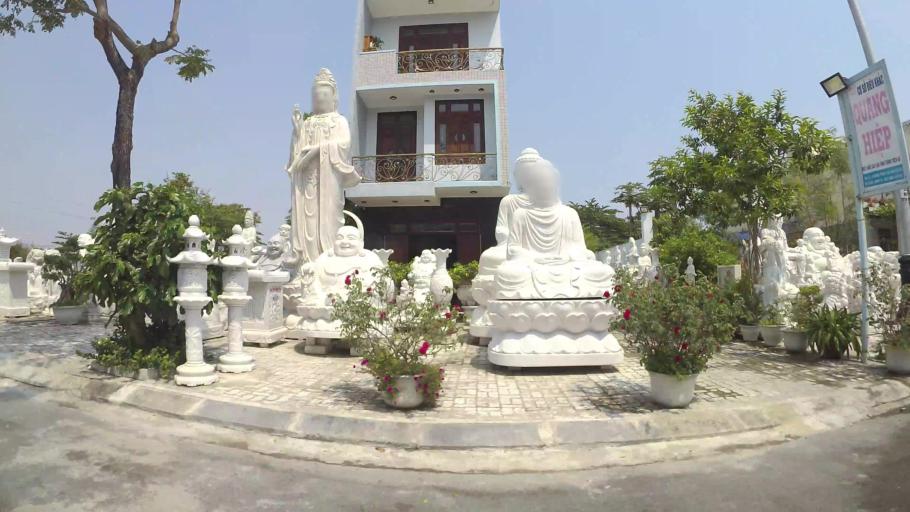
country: VN
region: Da Nang
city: Ngu Hanh Son
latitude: 16.0058
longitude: 108.2580
